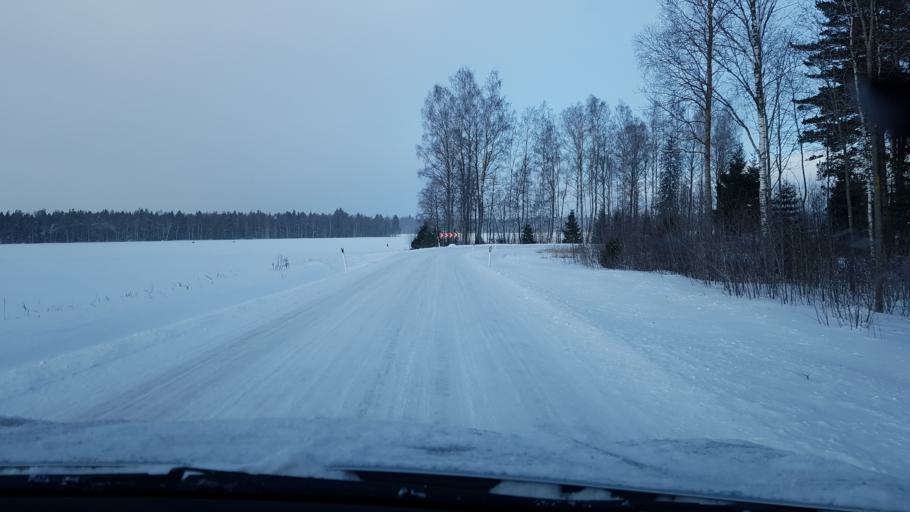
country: EE
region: Harju
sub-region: Nissi vald
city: Turba
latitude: 59.1967
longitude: 24.1390
